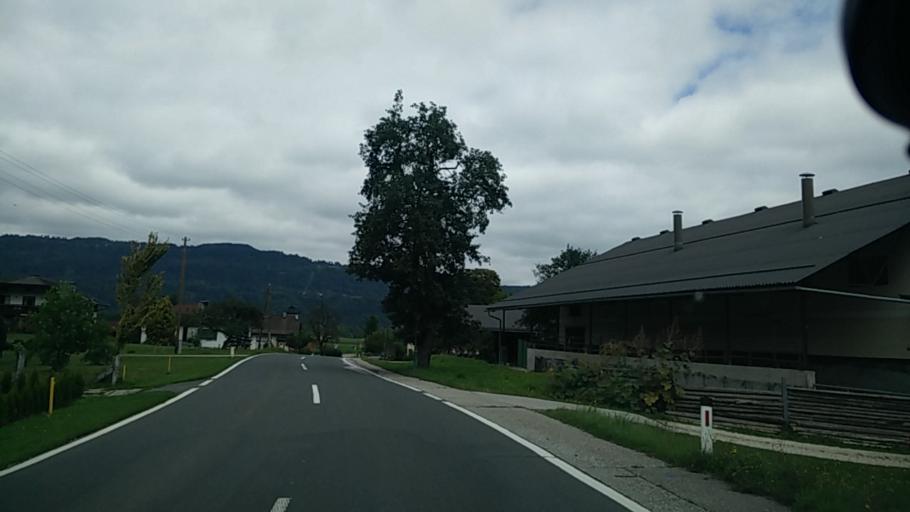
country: AT
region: Carinthia
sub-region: Politischer Bezirk Klagenfurt Land
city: Kottmannsdorf
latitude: 46.5276
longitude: 14.2108
